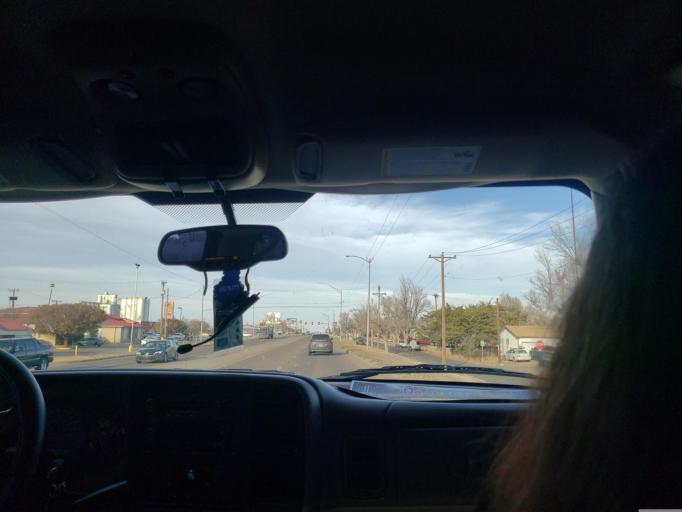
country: US
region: Oklahoma
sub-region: Texas County
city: Guymon
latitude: 36.6794
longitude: -101.4722
